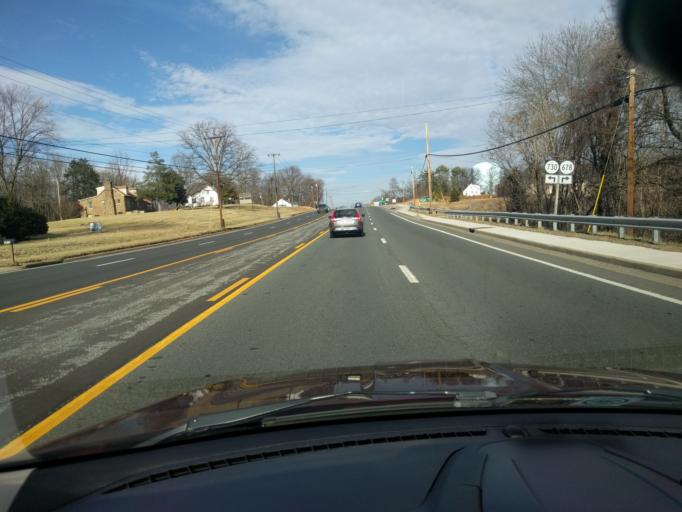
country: US
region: Virginia
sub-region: Amherst County
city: Madison Heights
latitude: 37.4736
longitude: -79.1199
